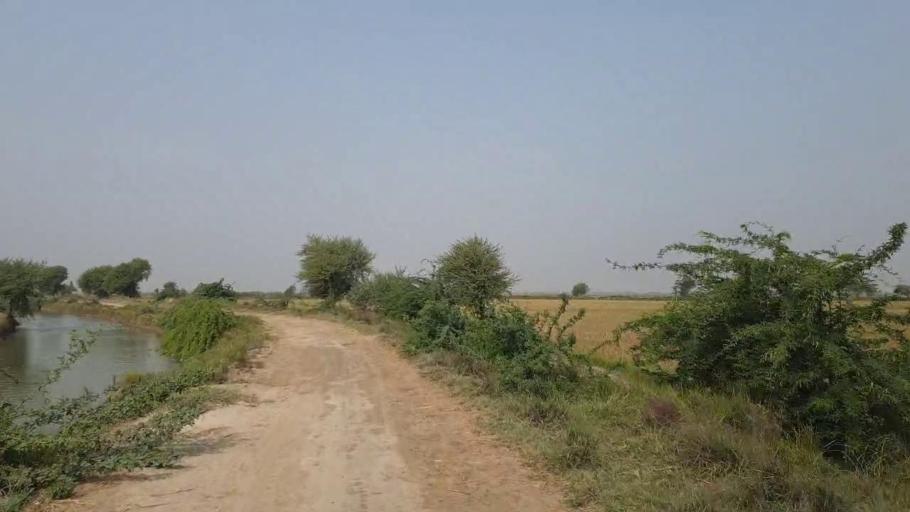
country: PK
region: Sindh
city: Kario
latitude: 24.8457
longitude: 68.5360
